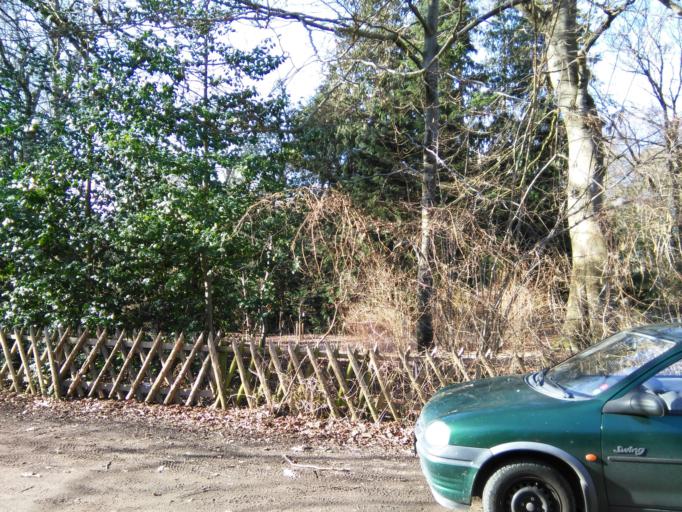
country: DK
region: Central Jutland
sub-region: Arhus Kommune
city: Arhus
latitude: 56.1252
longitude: 10.2041
